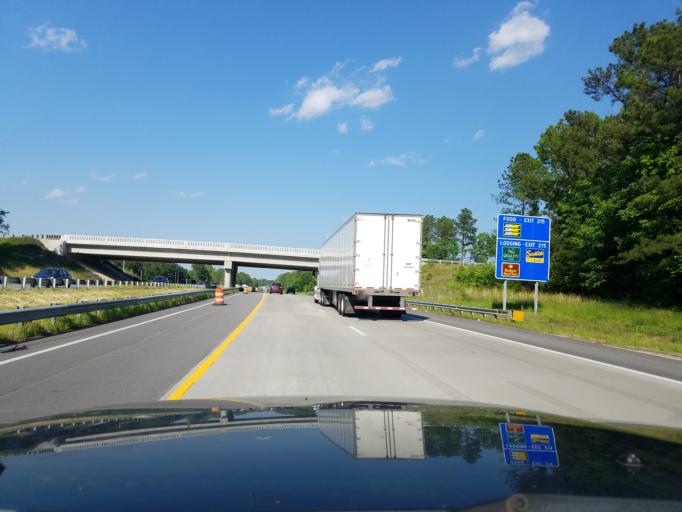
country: US
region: North Carolina
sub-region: Vance County
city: Henderson
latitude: 36.3397
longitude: -78.4117
